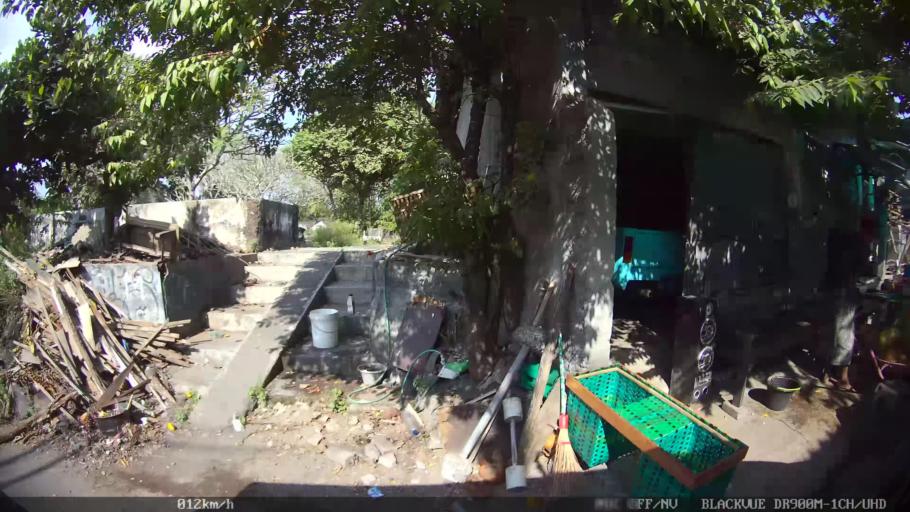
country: ID
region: Daerah Istimewa Yogyakarta
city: Sewon
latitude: -7.8324
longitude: 110.3952
